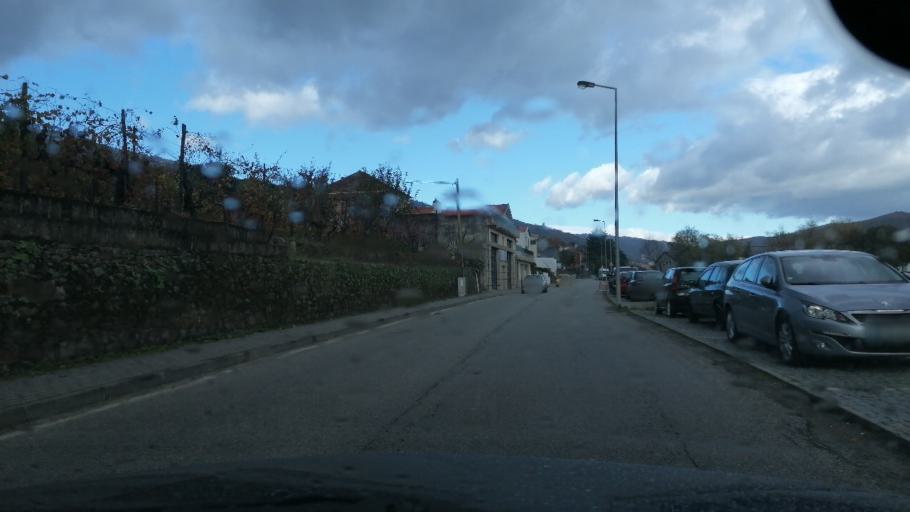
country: PT
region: Vila Real
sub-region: Peso da Regua
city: Godim
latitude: 41.1705
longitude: -7.7964
